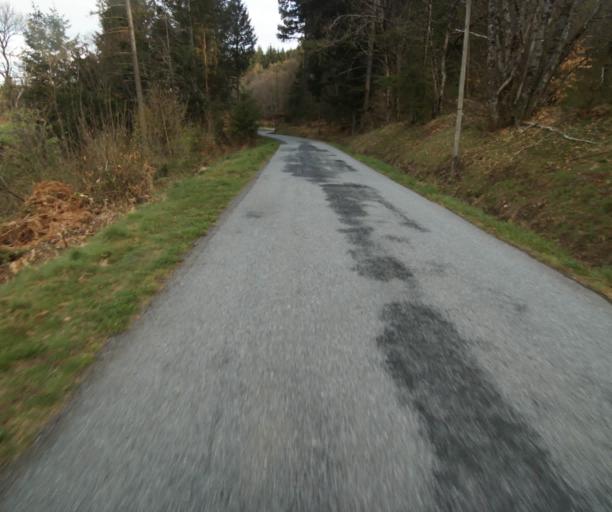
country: FR
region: Limousin
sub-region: Departement de la Correze
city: Correze
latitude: 45.4174
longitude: 1.8907
